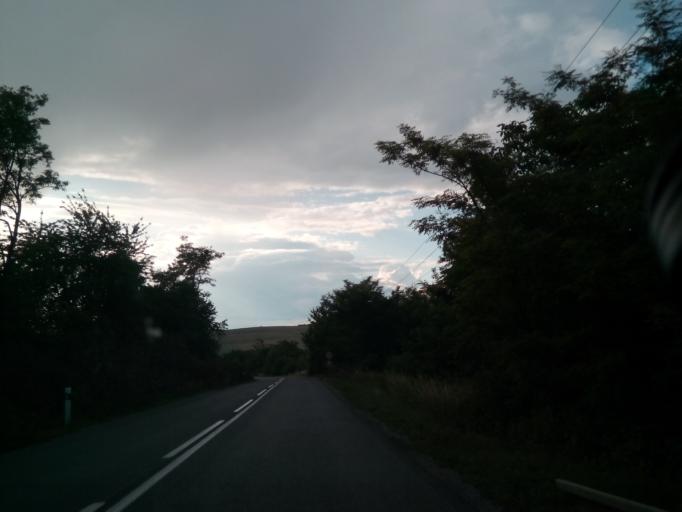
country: SK
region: Kosicky
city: Kosice
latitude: 48.6505
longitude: 21.4083
